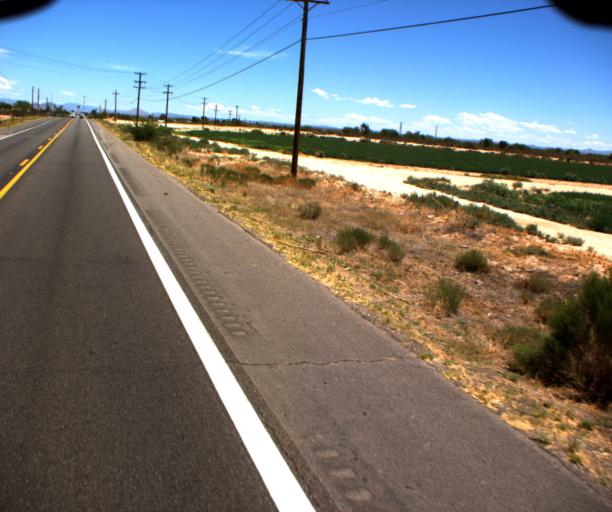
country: US
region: Arizona
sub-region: Pinal County
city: Florence
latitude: 33.0165
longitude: -111.3991
